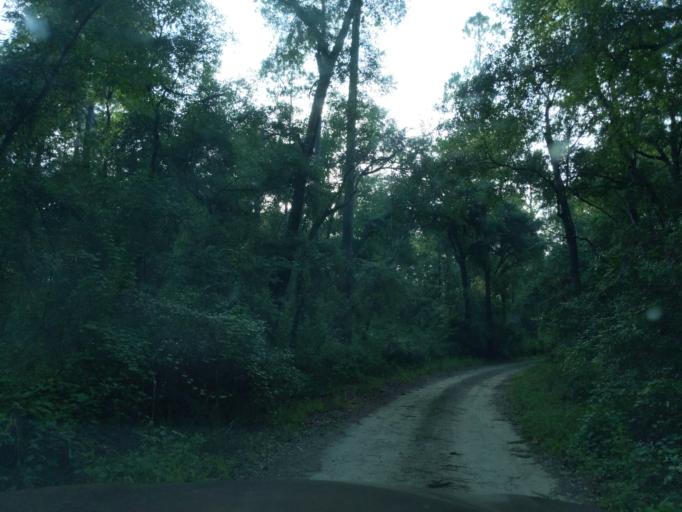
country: US
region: Florida
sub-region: Leon County
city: Tallahassee
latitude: 30.3668
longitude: -84.3630
